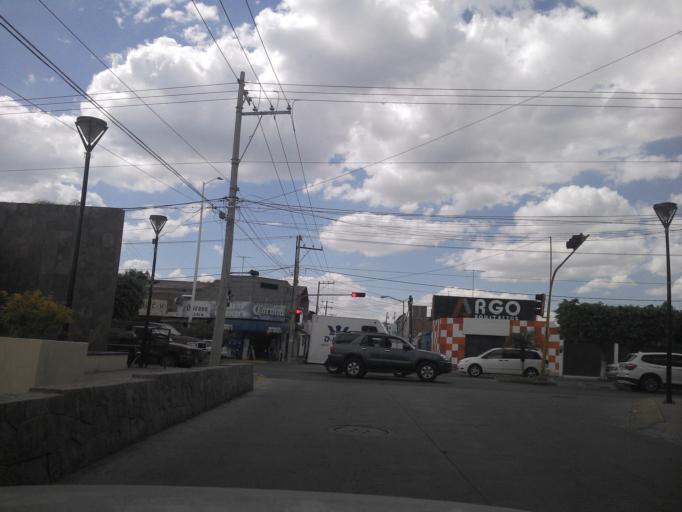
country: MX
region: Guanajuato
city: San Francisco del Rincon
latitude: 21.0284
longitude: -101.8602
